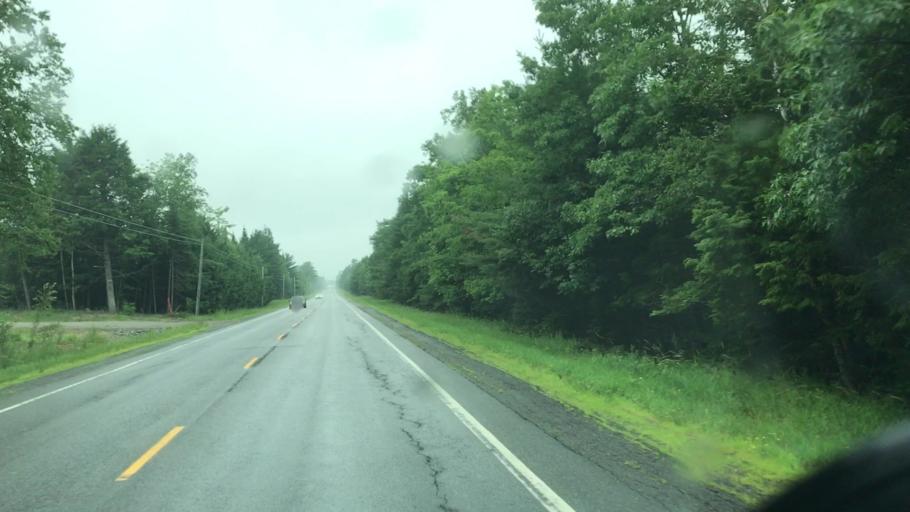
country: US
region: Maine
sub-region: Penobscot County
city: Enfield
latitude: 45.3118
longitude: -68.6070
